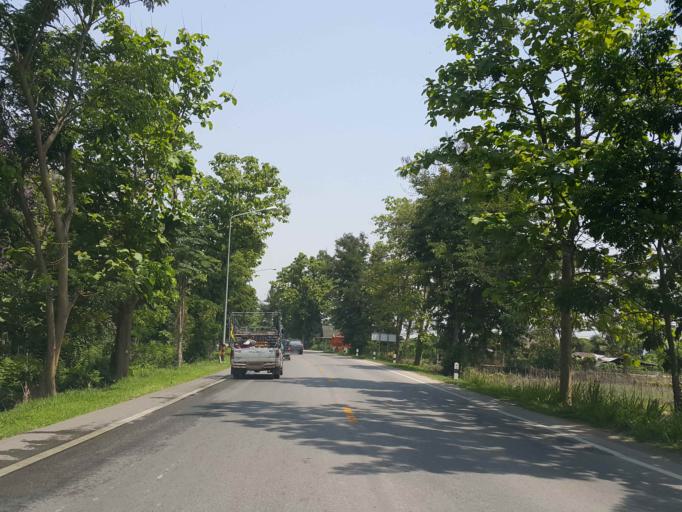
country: TH
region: Chiang Mai
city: Mae Taeng
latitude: 18.9974
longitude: 98.9769
